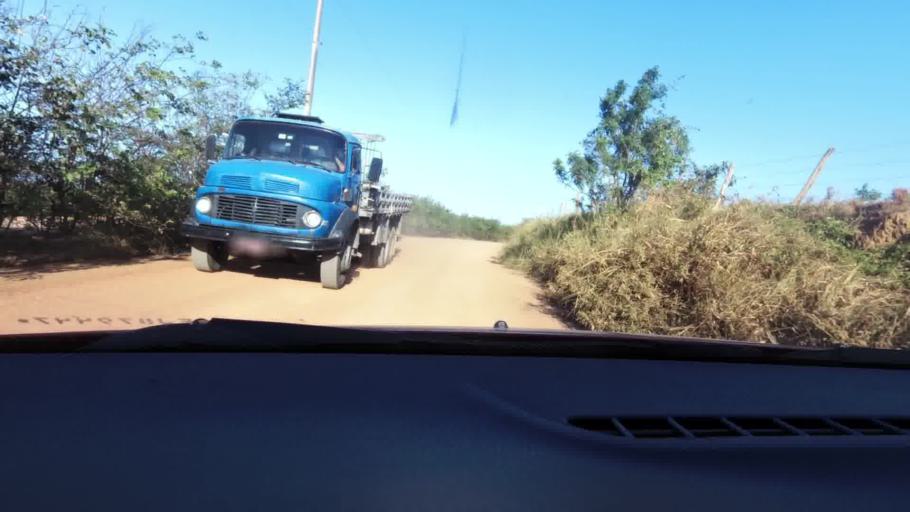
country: BR
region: Espirito Santo
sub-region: Guarapari
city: Guarapari
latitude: -20.5394
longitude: -40.4324
